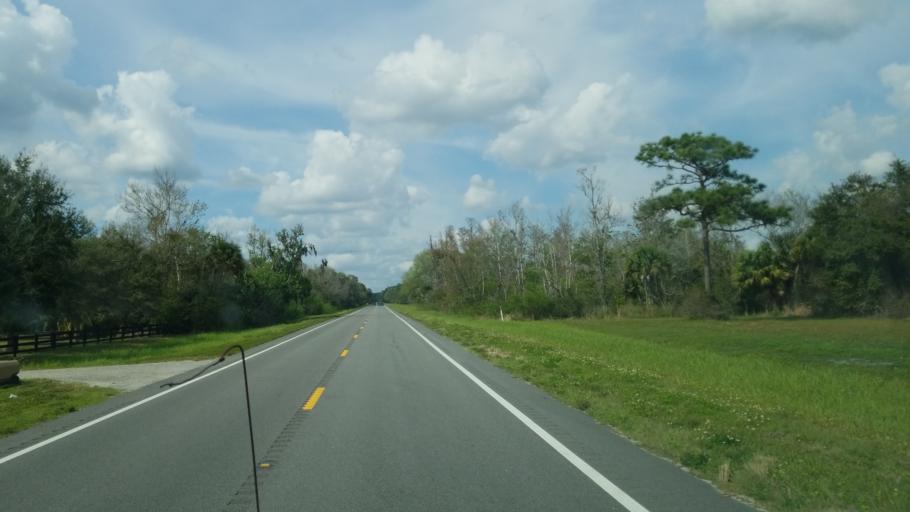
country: US
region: Florida
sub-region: Indian River County
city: Fellsmere
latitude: 27.7827
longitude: -80.9268
